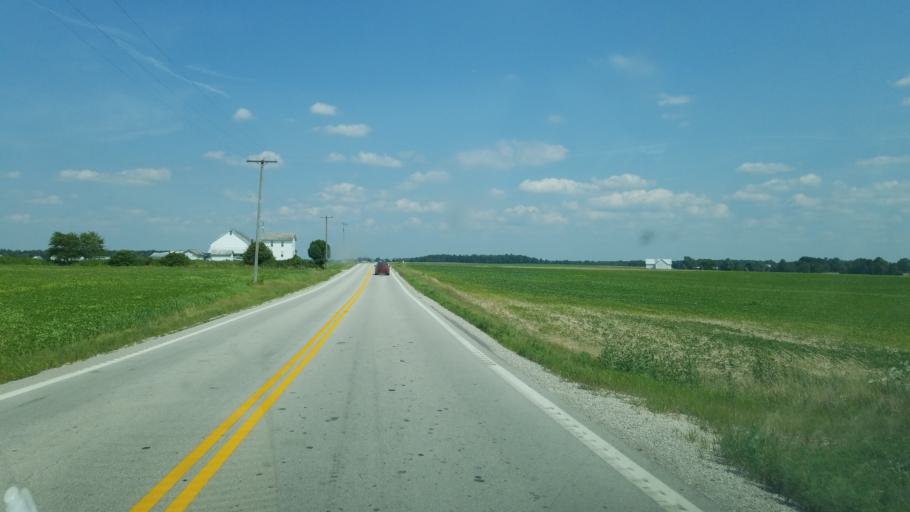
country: US
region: Ohio
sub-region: Huron County
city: Bellevue
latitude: 41.1245
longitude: -82.8707
